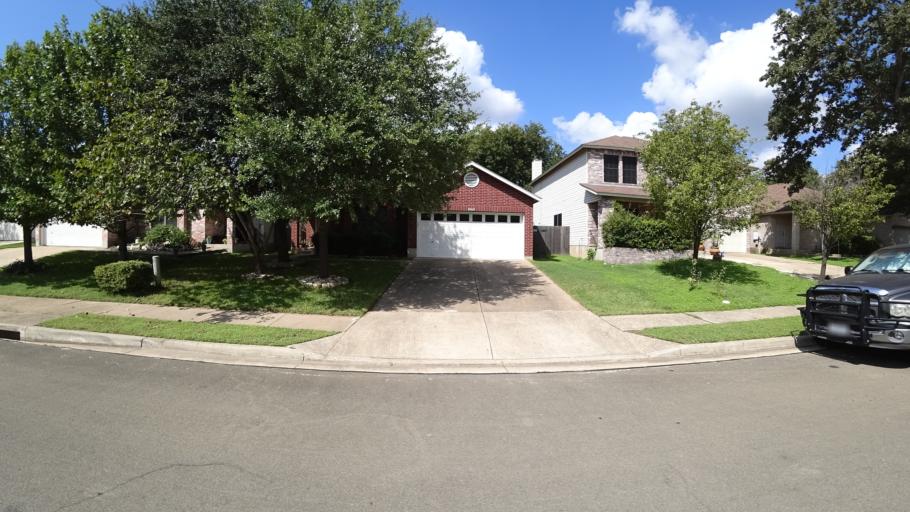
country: US
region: Texas
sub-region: Travis County
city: Manchaca
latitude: 30.1868
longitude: -97.8149
